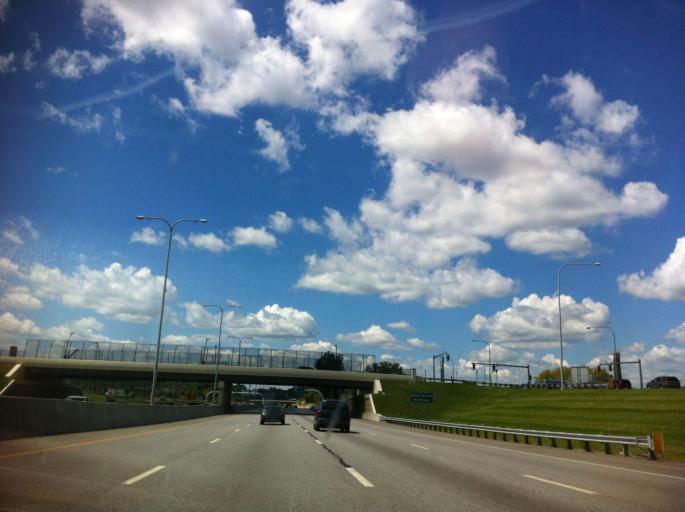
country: US
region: Ohio
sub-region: Lucas County
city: Toledo
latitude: 41.6791
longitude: -83.5895
